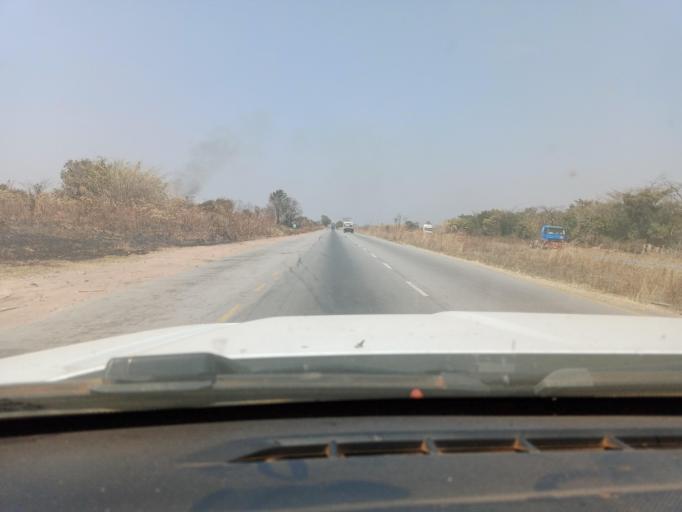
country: ZM
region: Copperbelt
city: Luanshya
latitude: -12.9972
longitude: 28.4210
